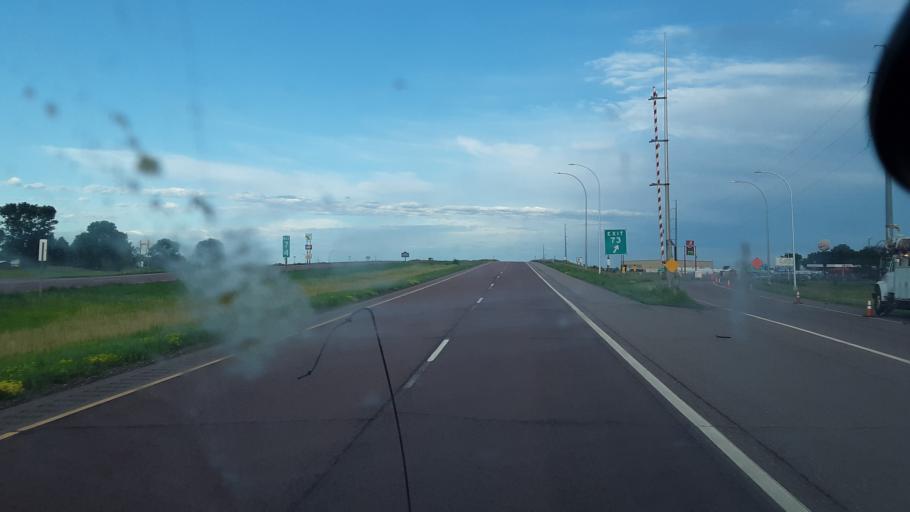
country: US
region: Minnesota
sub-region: Jackson County
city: Jackson
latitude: 43.6413
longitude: -94.9913
